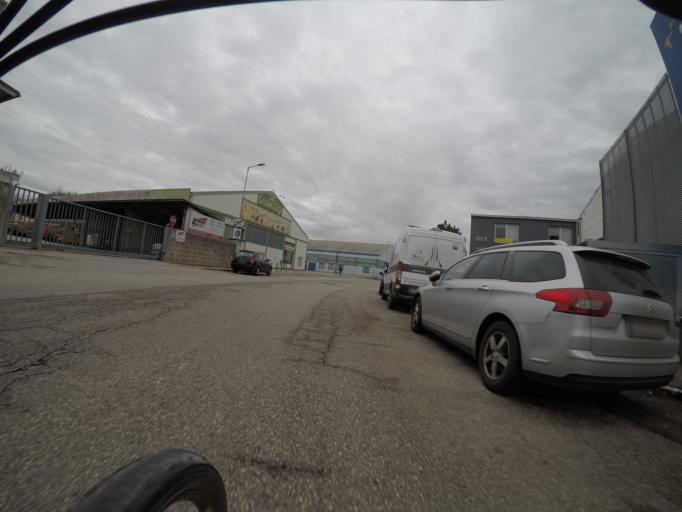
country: AT
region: Lower Austria
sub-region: Politischer Bezirk Modling
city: Brunn am Gebirge
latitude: 48.1100
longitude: 16.3101
